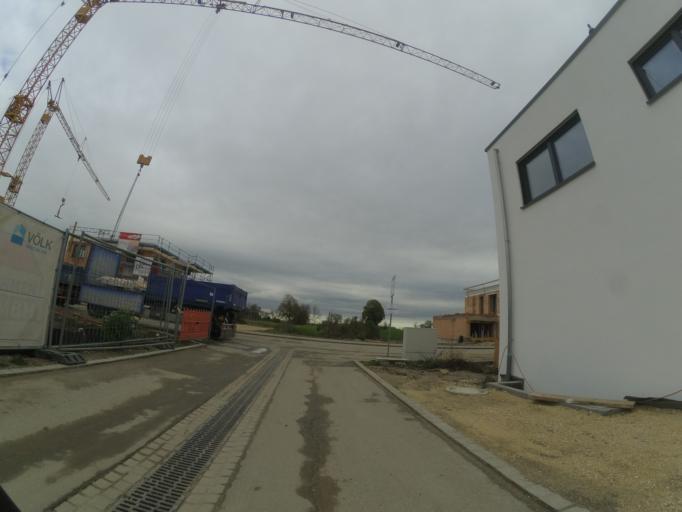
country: DE
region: Bavaria
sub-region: Swabia
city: Neu-Ulm
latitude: 48.3704
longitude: 10.0183
